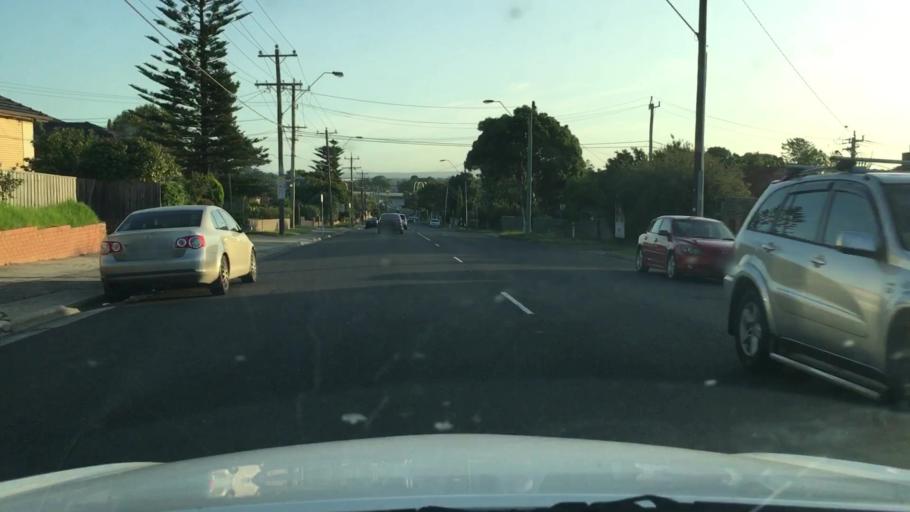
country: AU
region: Victoria
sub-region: Greater Dandenong
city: Dandenong
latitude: -37.9688
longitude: 145.1868
